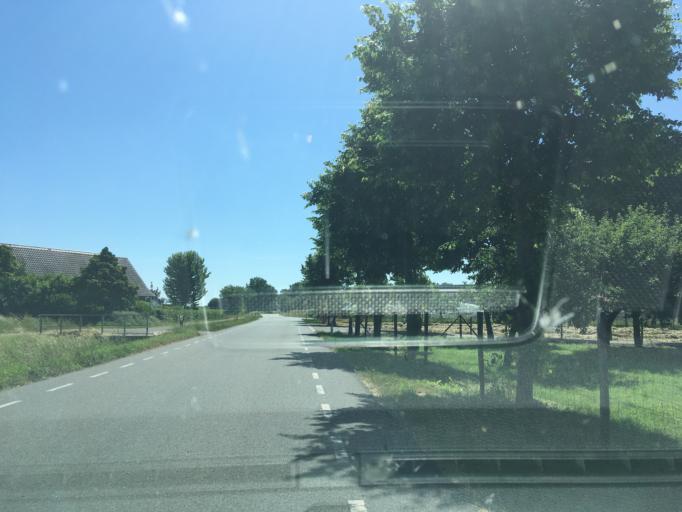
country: DE
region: North Rhine-Westphalia
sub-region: Regierungsbezirk Munster
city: Borken
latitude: 51.8214
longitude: 6.8033
